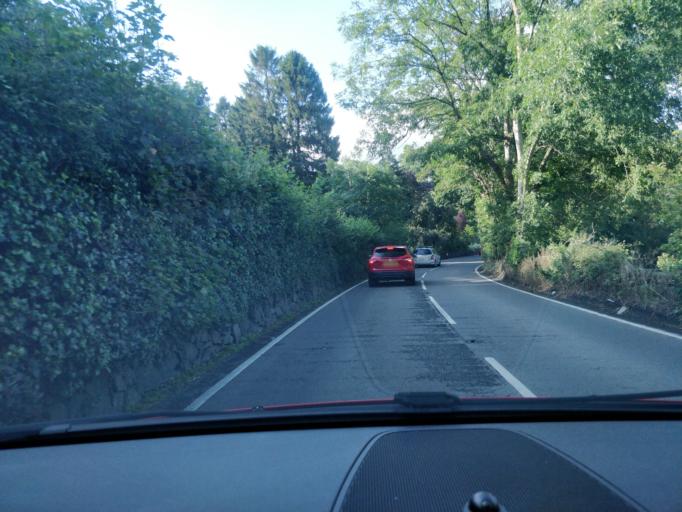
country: GB
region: Wales
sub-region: Conwy
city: Llanrwst
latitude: 53.1974
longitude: -3.8235
